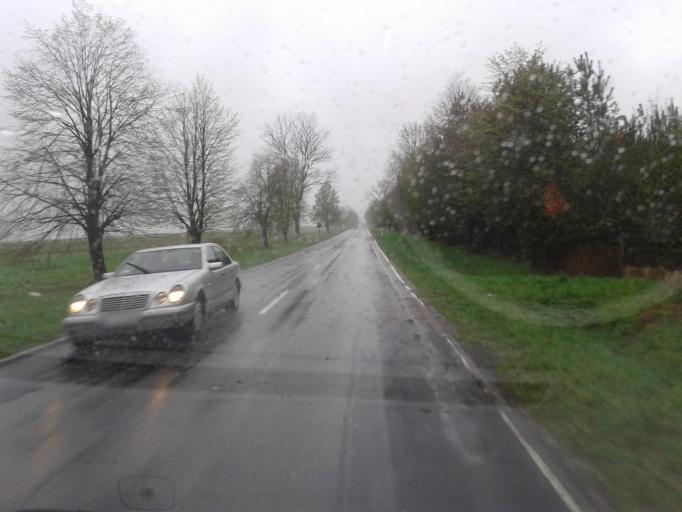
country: PL
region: Subcarpathian Voivodeship
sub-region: Powiat lubaczowski
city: Cieszanow
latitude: 50.2658
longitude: 23.1461
